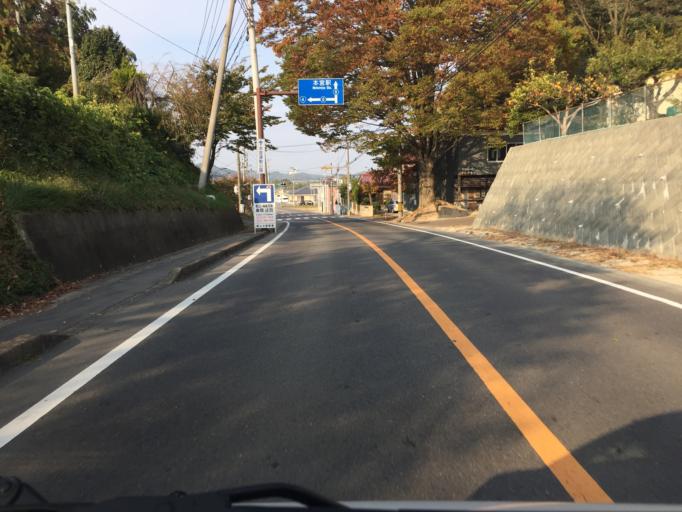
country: JP
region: Fukushima
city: Motomiya
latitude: 37.5015
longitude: 140.4014
